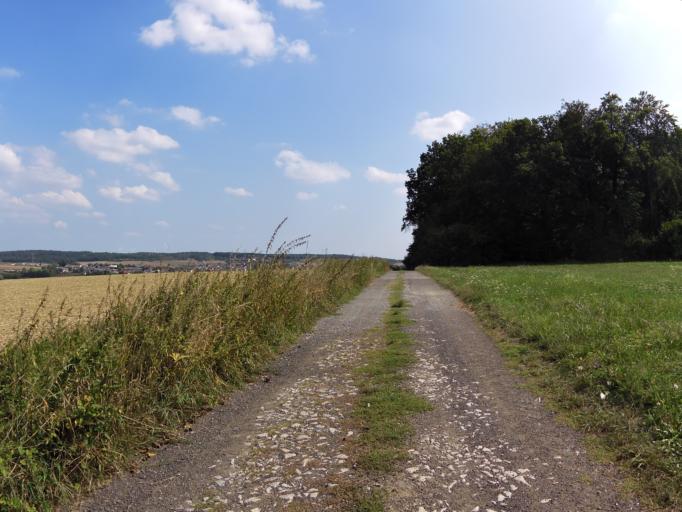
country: DE
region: Bavaria
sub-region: Regierungsbezirk Unterfranken
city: Kleinrinderfeld
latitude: 49.7062
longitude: 9.8262
